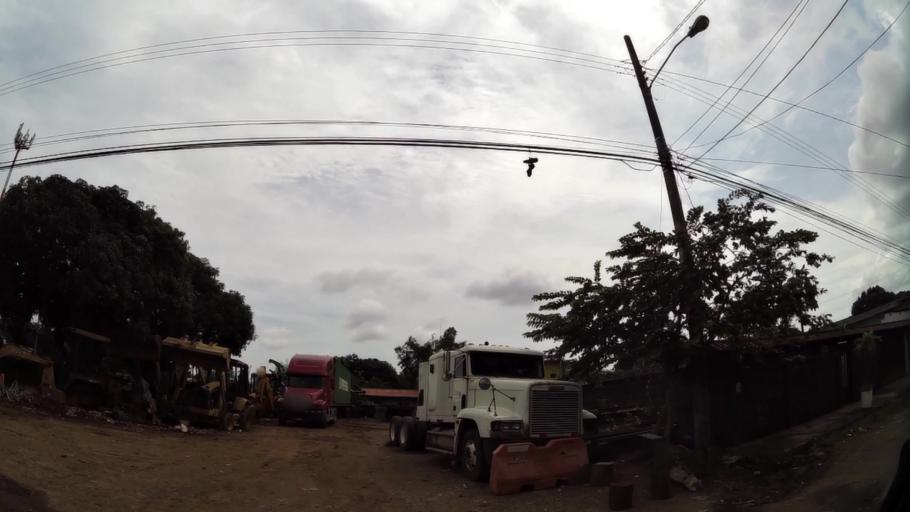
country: PA
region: Panama
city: San Miguelito
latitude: 9.0503
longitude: -79.4261
